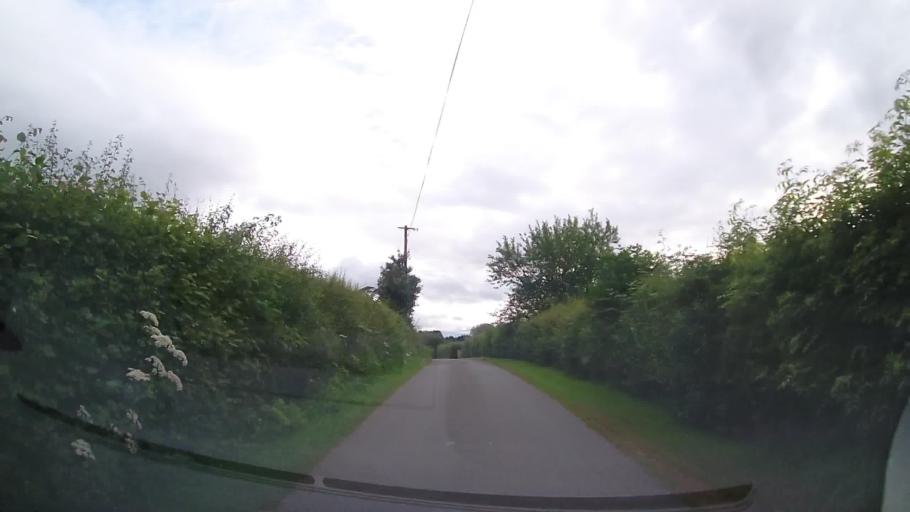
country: GB
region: England
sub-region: Shropshire
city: Prees
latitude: 52.9136
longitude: -2.6985
